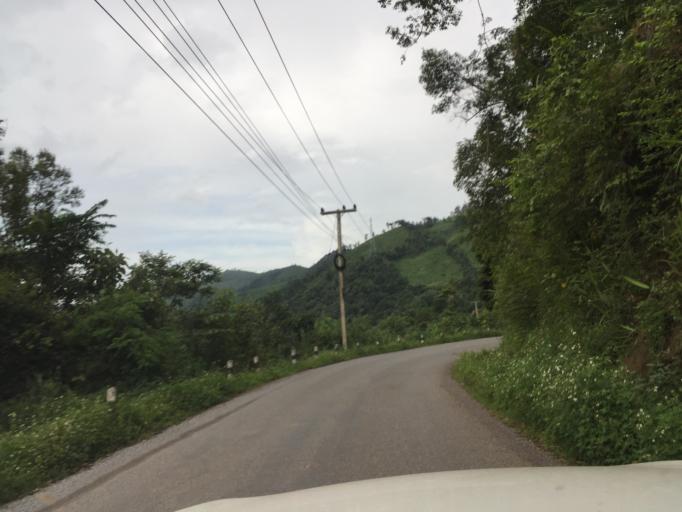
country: LA
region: Phongsali
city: Phongsali
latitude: 21.3418
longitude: 102.0489
